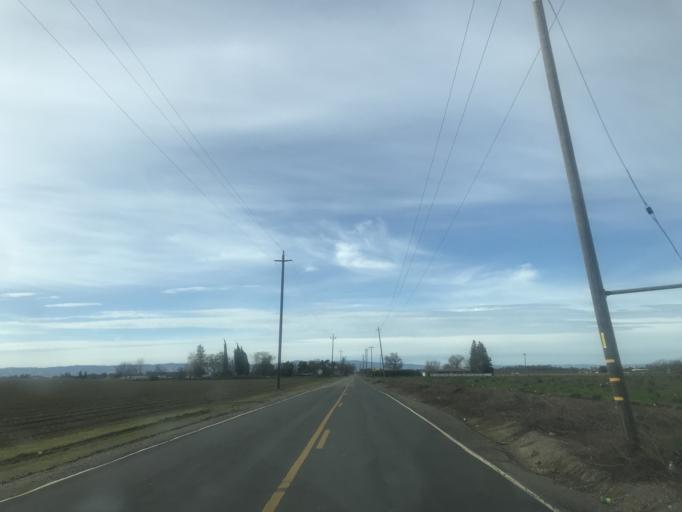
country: US
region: California
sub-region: Yolo County
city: Woodland
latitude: 38.6634
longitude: -121.8359
